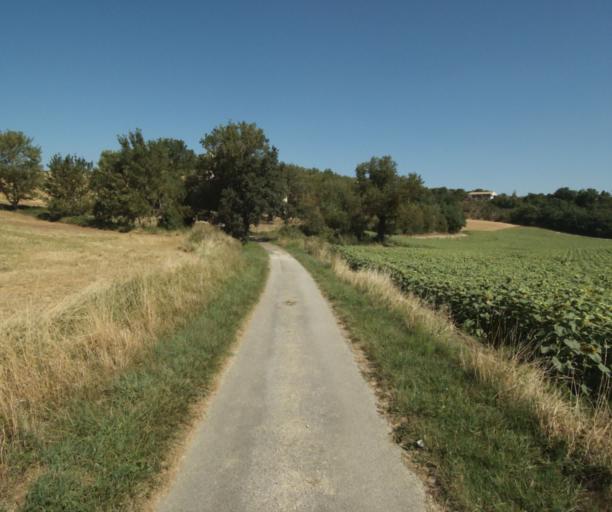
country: FR
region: Midi-Pyrenees
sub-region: Departement de la Haute-Garonne
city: Saint-Felix-Lauragais
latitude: 43.5071
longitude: 1.9363
